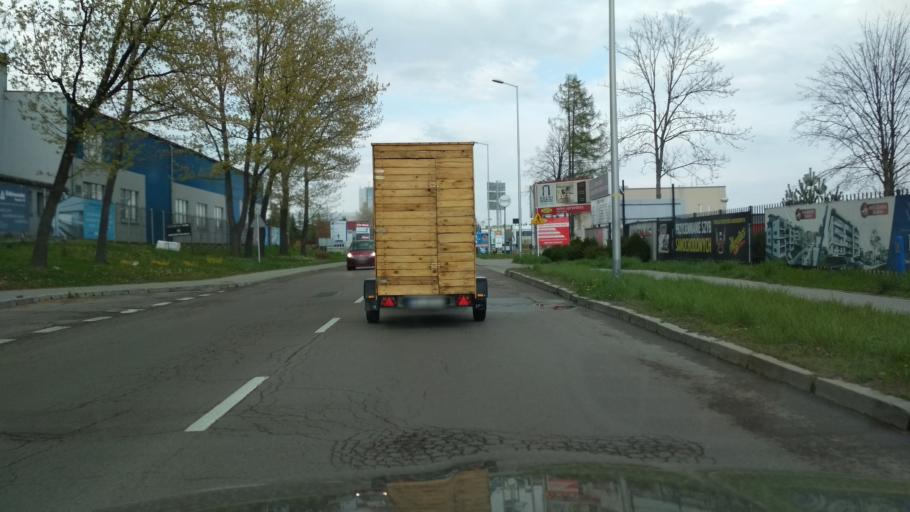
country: PL
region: Subcarpathian Voivodeship
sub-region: Rzeszow
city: Rzeszow
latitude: 50.0229
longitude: 21.9705
